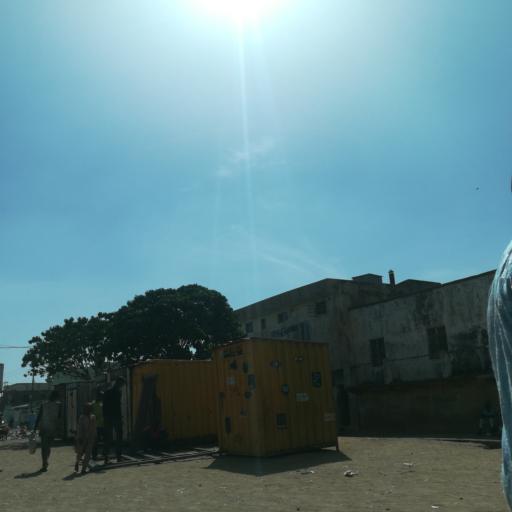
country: NG
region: Kano
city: Kano
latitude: 11.9943
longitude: 8.5311
